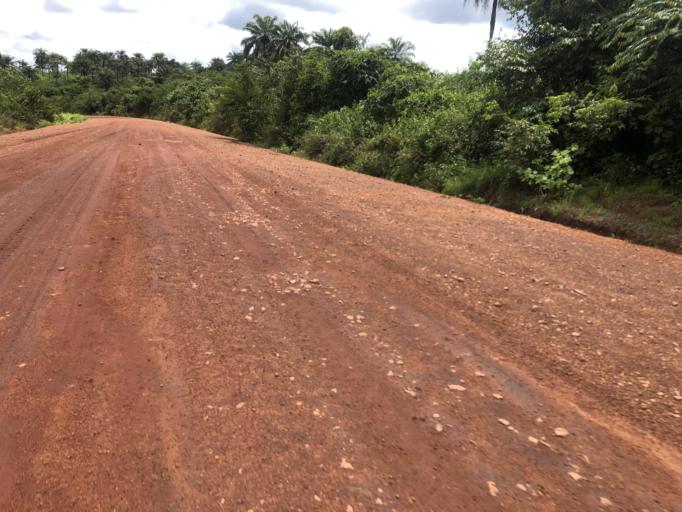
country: SL
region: Northern Province
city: Port Loko
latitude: 8.7167
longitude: -12.8362
